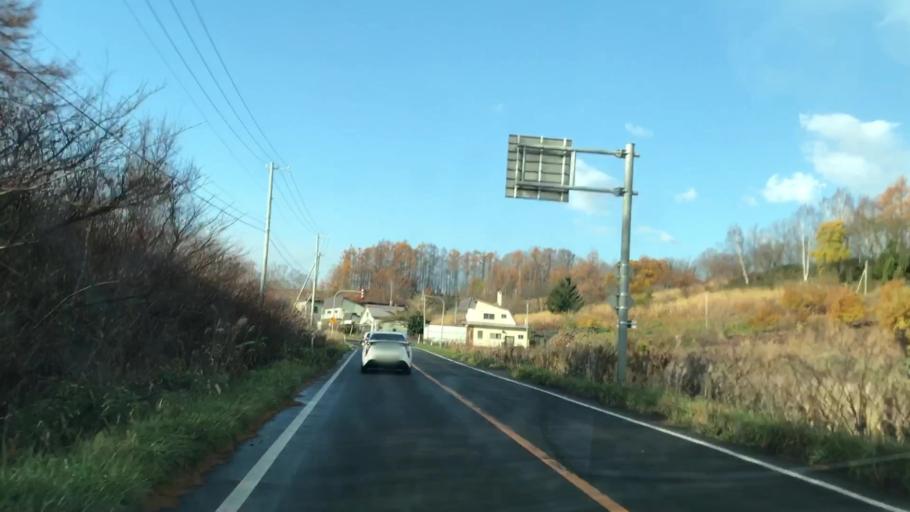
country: JP
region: Hokkaido
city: Yoichi
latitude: 43.1910
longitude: 140.8390
